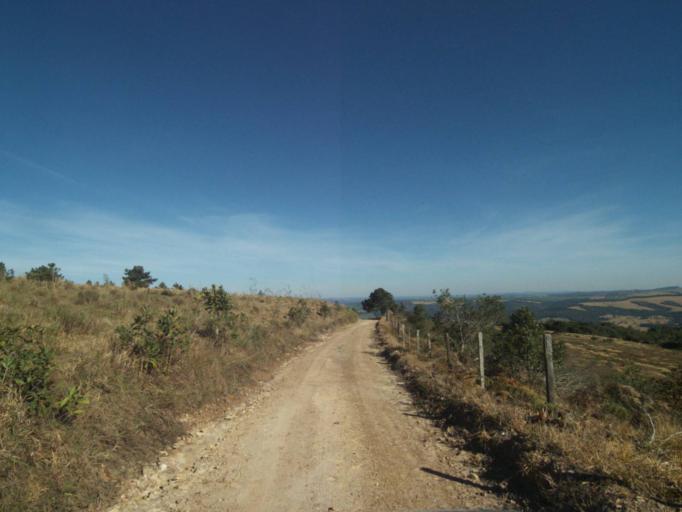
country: BR
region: Parana
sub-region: Tibagi
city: Tibagi
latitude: -24.5778
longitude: -50.4820
